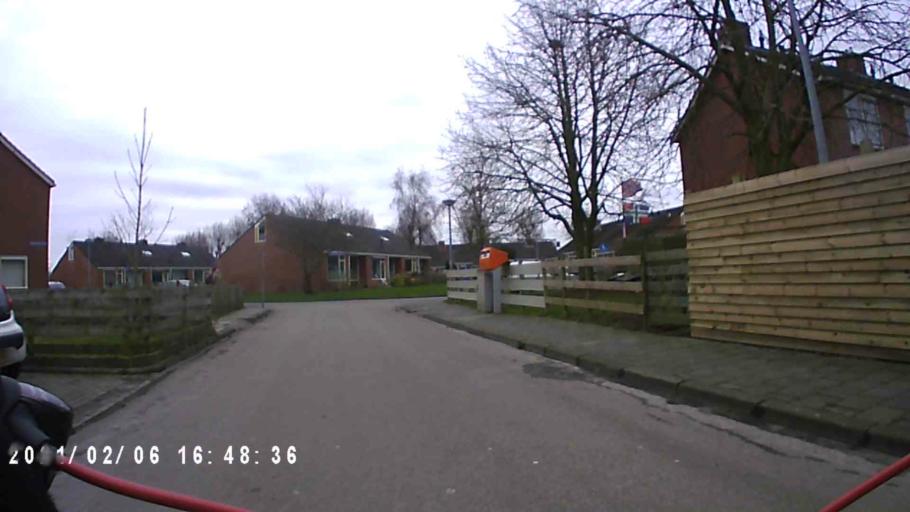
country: NL
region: Groningen
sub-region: Gemeente Appingedam
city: Appingedam
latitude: 53.4147
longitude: 6.7327
